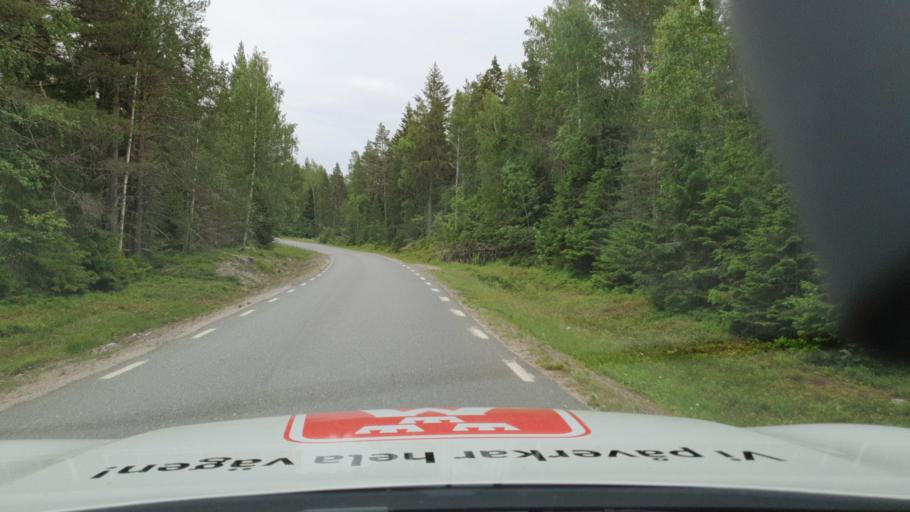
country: SE
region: Vaesterbotten
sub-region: Nordmalings Kommun
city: Nordmaling
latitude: 63.4346
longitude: 19.4721
